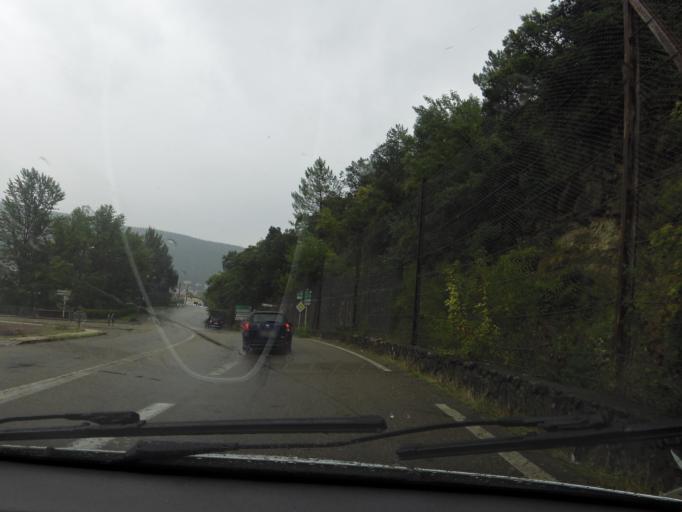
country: FR
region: Languedoc-Roussillon
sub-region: Departement du Gard
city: Les Salles-du-Gardon
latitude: 44.2066
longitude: 4.0277
